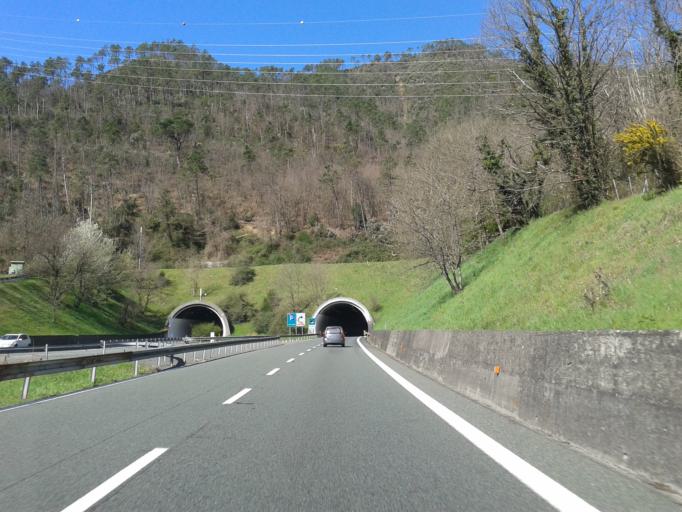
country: IT
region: Liguria
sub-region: Provincia di La Spezia
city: Beverino
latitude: 44.2060
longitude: 9.7828
